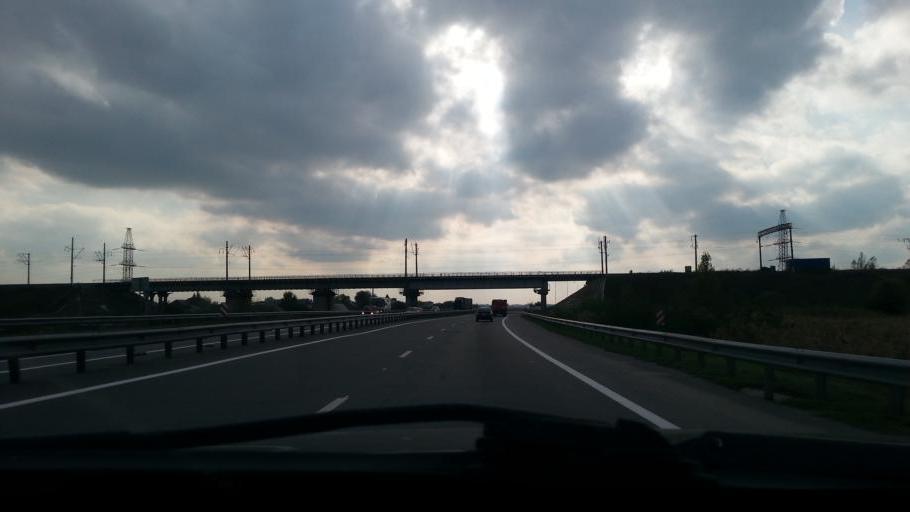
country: RU
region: Rostov
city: Bataysk
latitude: 47.1450
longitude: 39.7006
